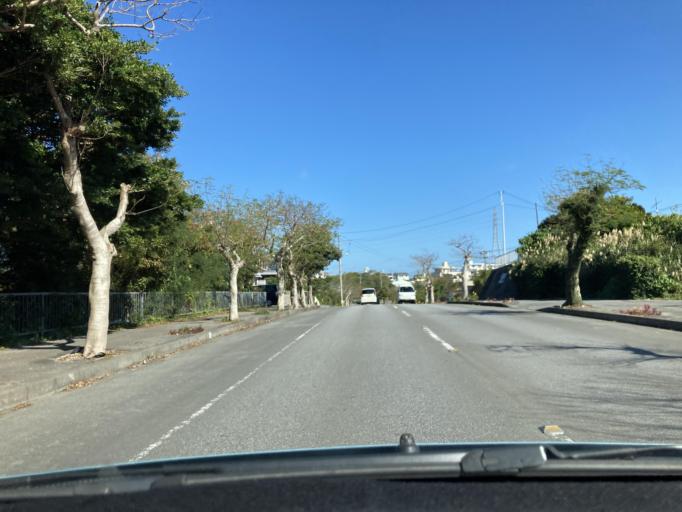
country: JP
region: Okinawa
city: Gushikawa
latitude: 26.3806
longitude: 127.8679
